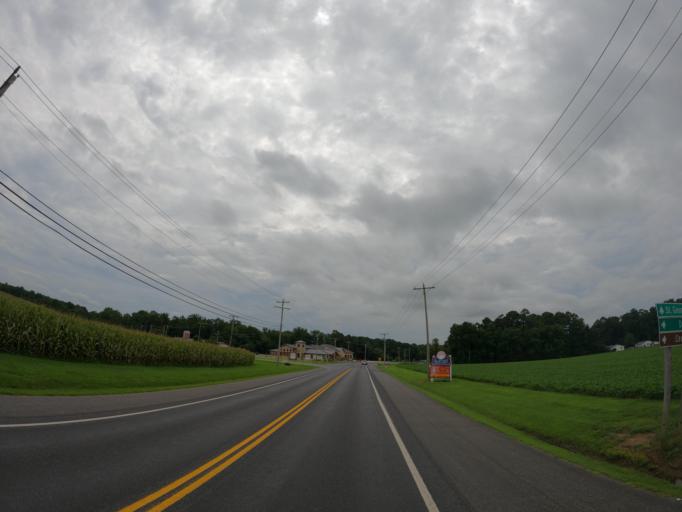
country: US
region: Maryland
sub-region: Saint Mary's County
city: Lexington Park
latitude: 38.1918
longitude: -76.5134
